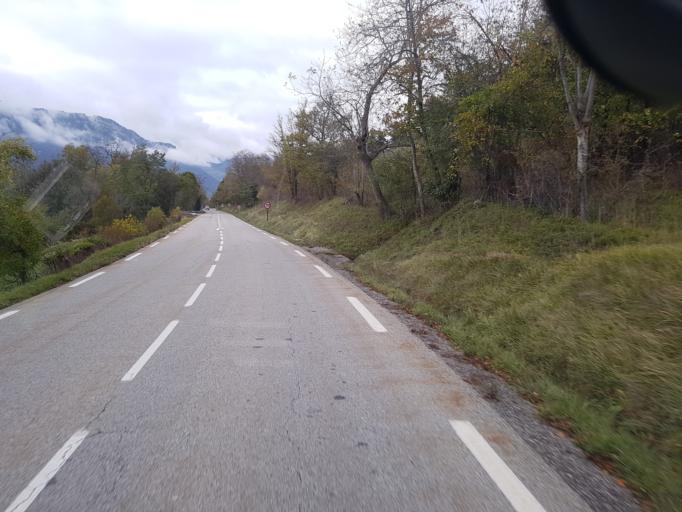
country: FR
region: Rhone-Alpes
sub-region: Departement de l'Isere
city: Le Gua
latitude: 44.9611
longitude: 5.6367
